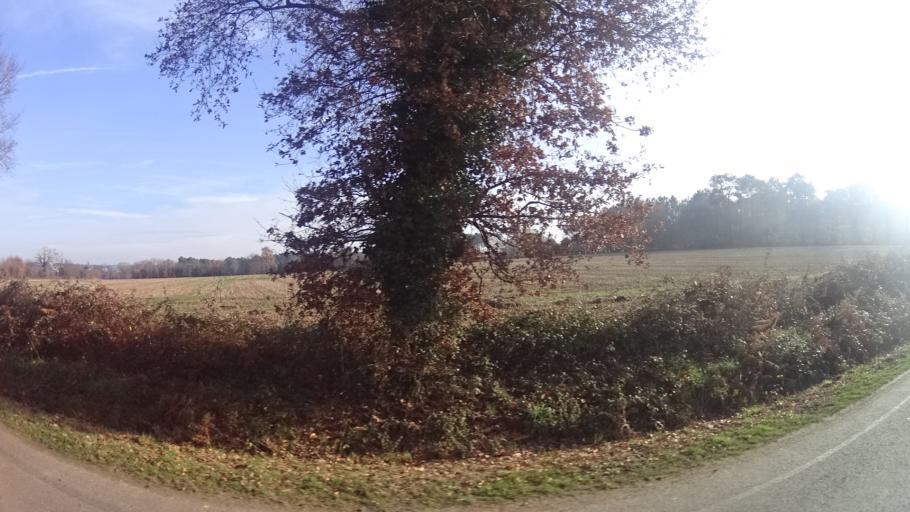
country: FR
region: Brittany
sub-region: Departement du Morbihan
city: Allaire
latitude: 47.6062
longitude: -2.1476
